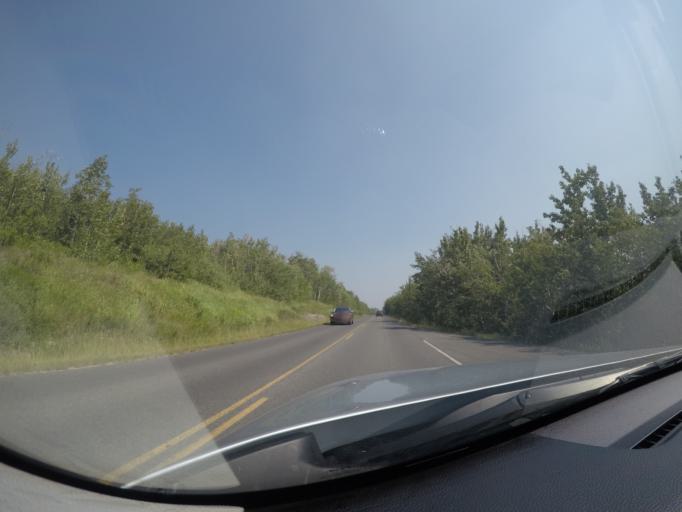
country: US
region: Montana
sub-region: Glacier County
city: North Browning
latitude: 48.7387
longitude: -113.4578
